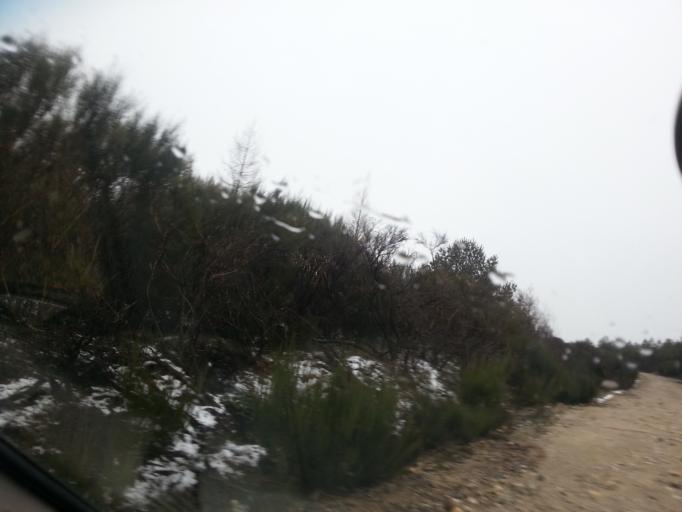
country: PT
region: Guarda
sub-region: Celorico da Beira
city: Celorico da Beira
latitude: 40.5275
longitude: -7.4497
